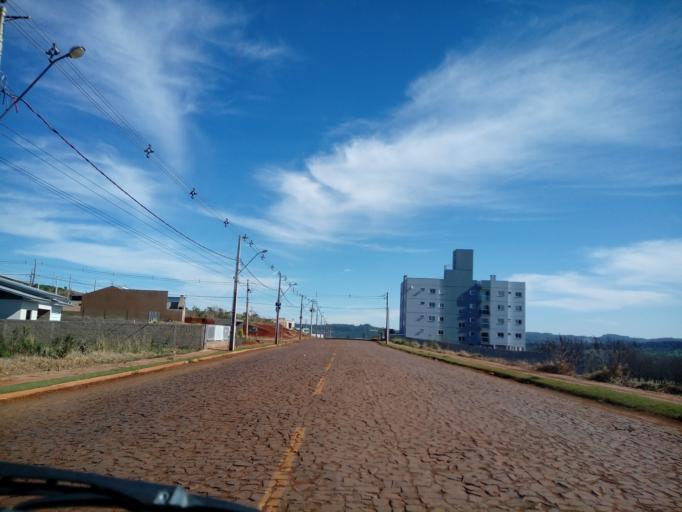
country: BR
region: Santa Catarina
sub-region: Chapeco
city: Chapeco
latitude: -27.0385
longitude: -52.6206
